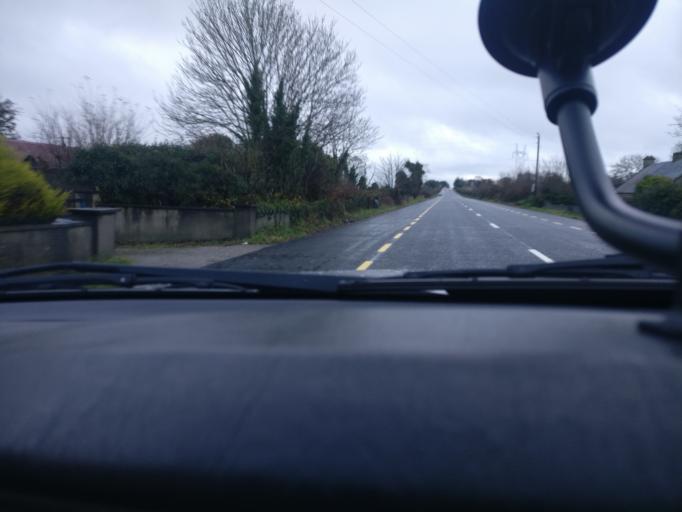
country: IE
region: Leinster
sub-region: An Mhi
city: Enfield
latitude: 53.4240
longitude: -6.8726
